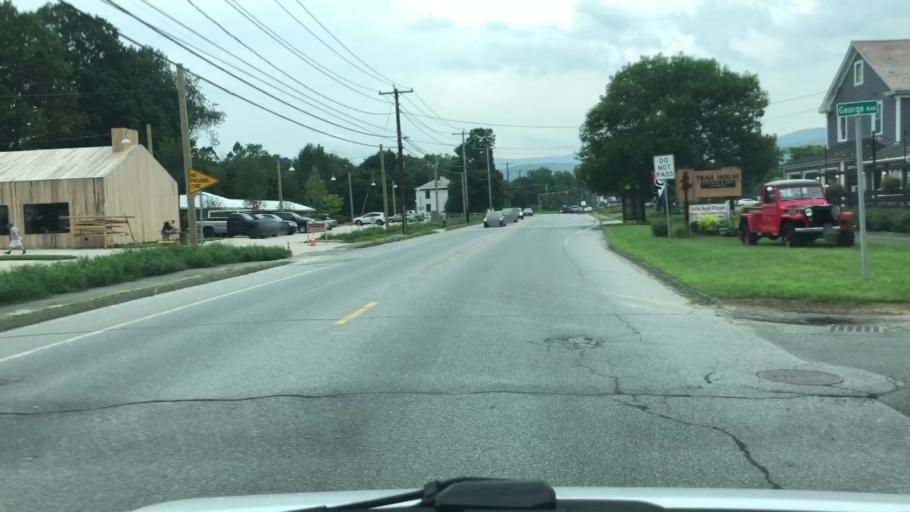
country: US
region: Massachusetts
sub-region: Berkshire County
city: Williamstown
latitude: 42.7006
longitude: -73.1673
